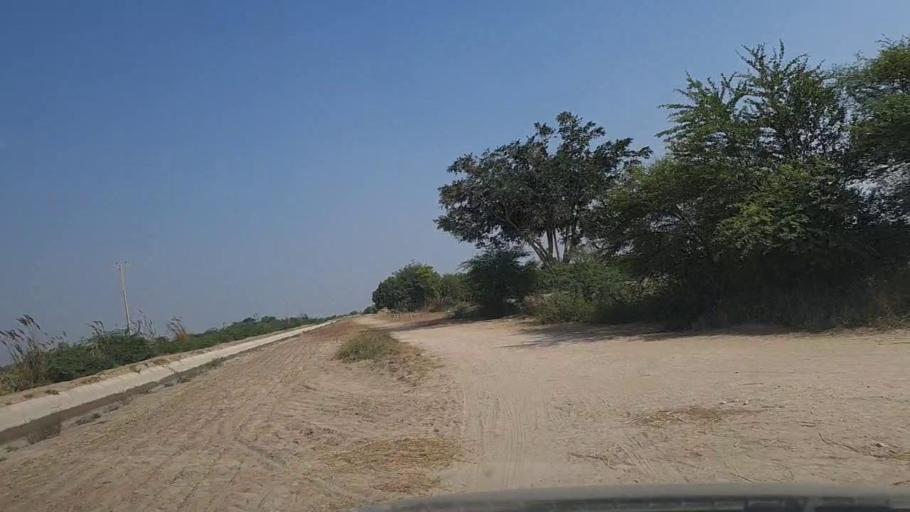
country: PK
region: Sindh
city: Mirpur Sakro
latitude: 24.5217
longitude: 67.8082
